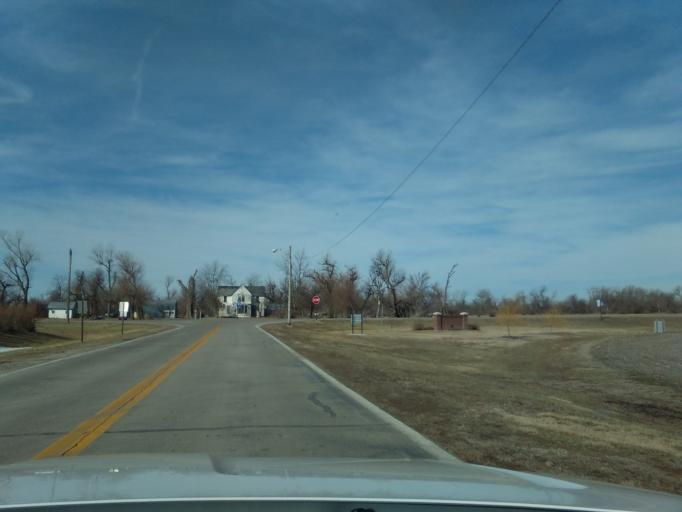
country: US
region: Nebraska
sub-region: Saline County
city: Friend
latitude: 40.7784
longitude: -97.2911
